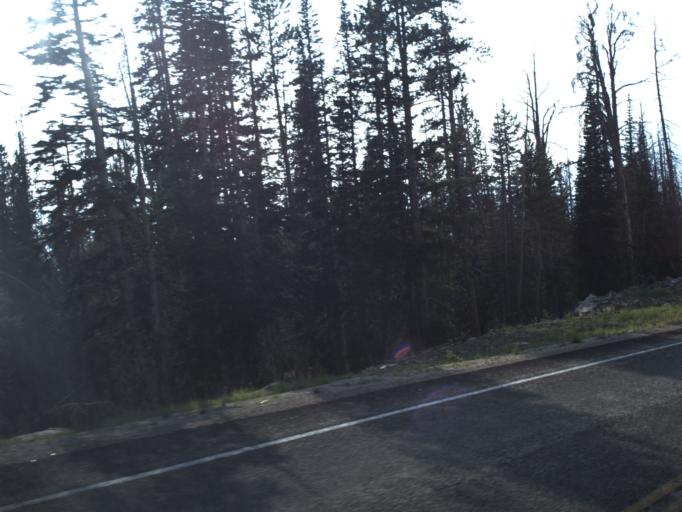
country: US
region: Utah
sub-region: Summit County
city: Kamas
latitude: 40.6818
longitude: -110.9268
